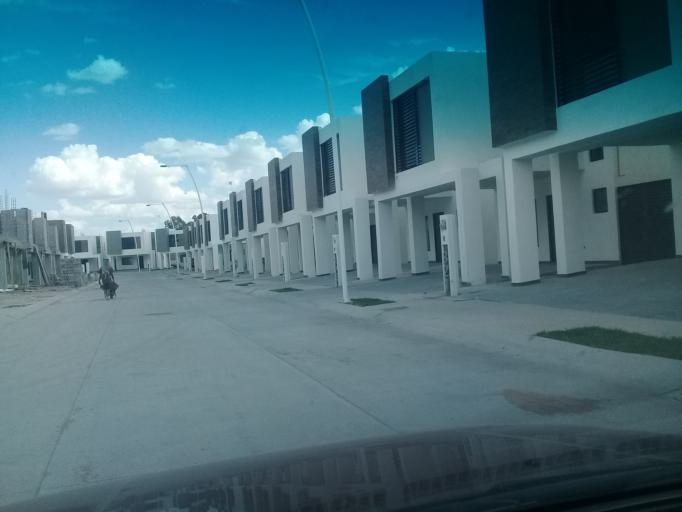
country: MX
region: Aguascalientes
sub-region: Aguascalientes
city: San Sebastian [Fraccionamiento]
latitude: 21.8333
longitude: -102.3141
